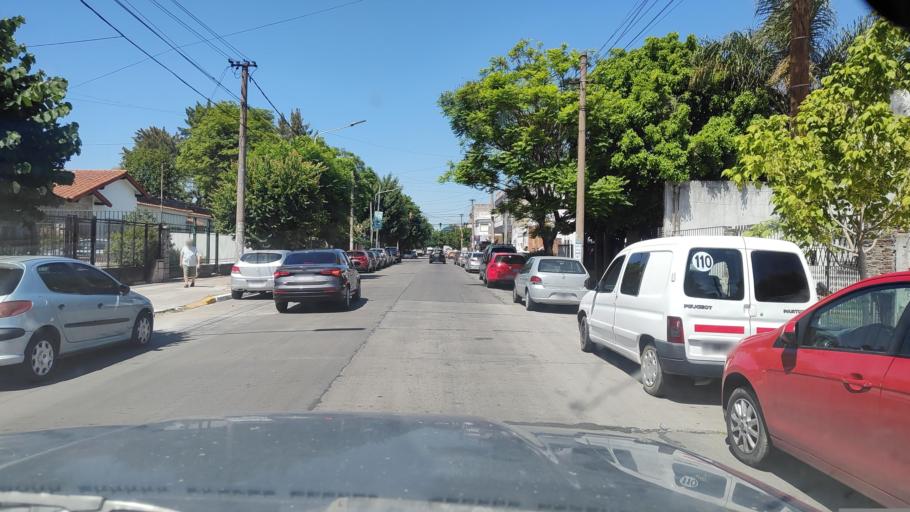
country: AR
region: Buenos Aires
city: San Justo
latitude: -34.6805
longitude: -58.5632
